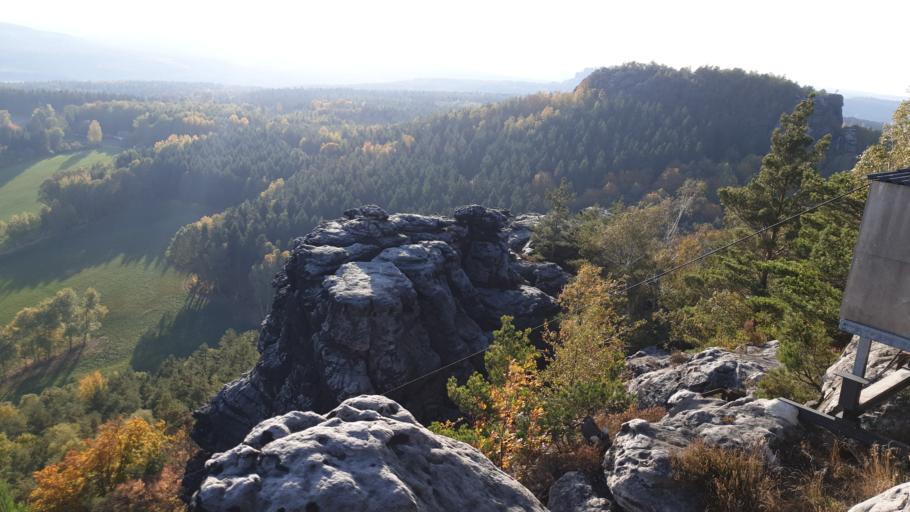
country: DE
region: Saxony
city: Kurort Gohrisch
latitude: 50.9009
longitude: 14.1201
